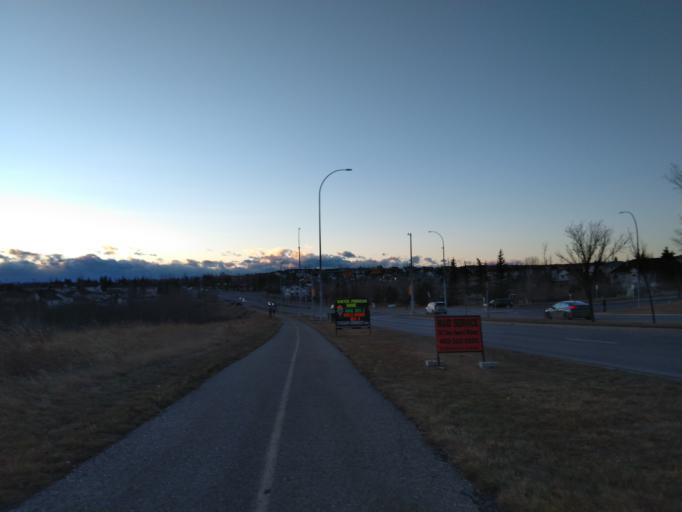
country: CA
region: Alberta
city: Calgary
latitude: 51.1253
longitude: -114.2374
